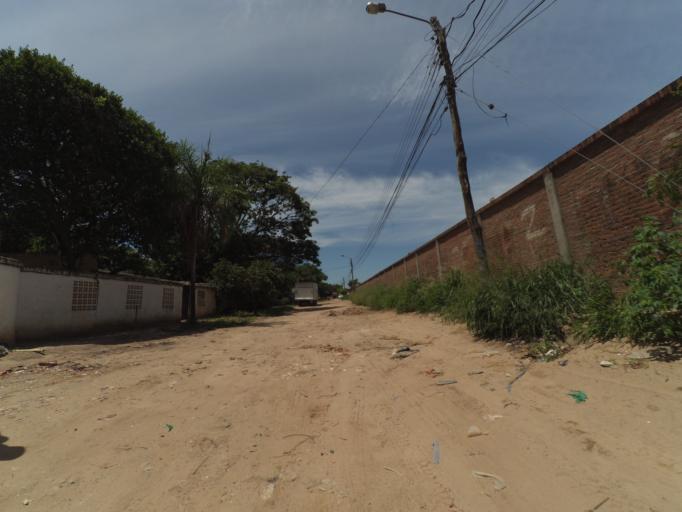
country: BO
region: Santa Cruz
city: Santa Cruz de la Sierra
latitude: -17.8101
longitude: -63.2229
